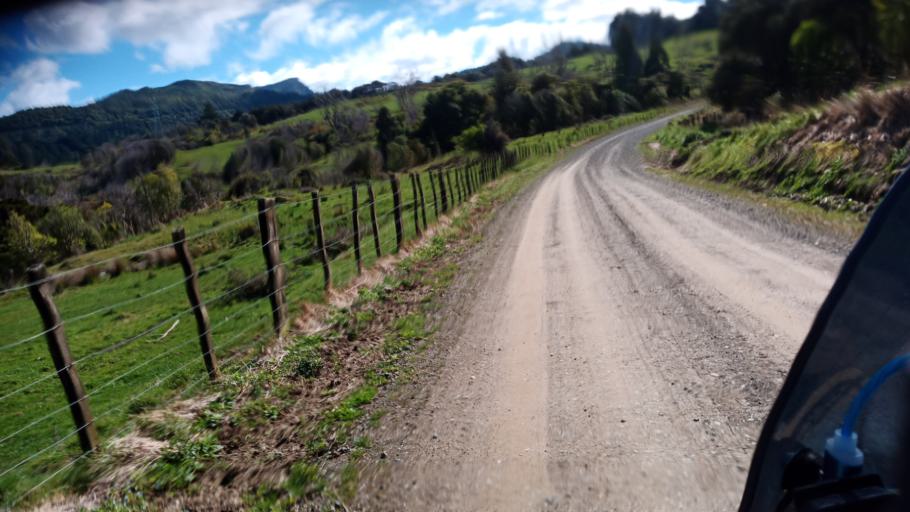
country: NZ
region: Hawke's Bay
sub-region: Wairoa District
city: Wairoa
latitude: -38.8185
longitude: 177.1574
